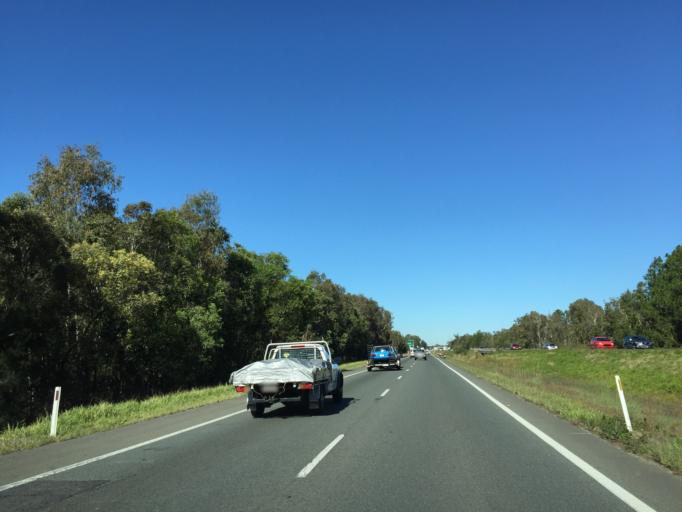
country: AU
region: Queensland
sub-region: Moreton Bay
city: Caboolture
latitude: -27.0556
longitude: 152.9770
